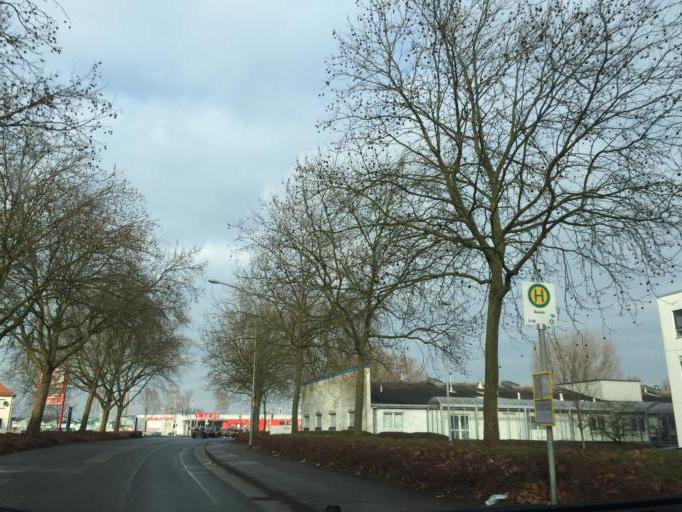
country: DE
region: North Rhine-Westphalia
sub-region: Regierungsbezirk Dusseldorf
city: Kleve
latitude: 51.7985
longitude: 6.1398
